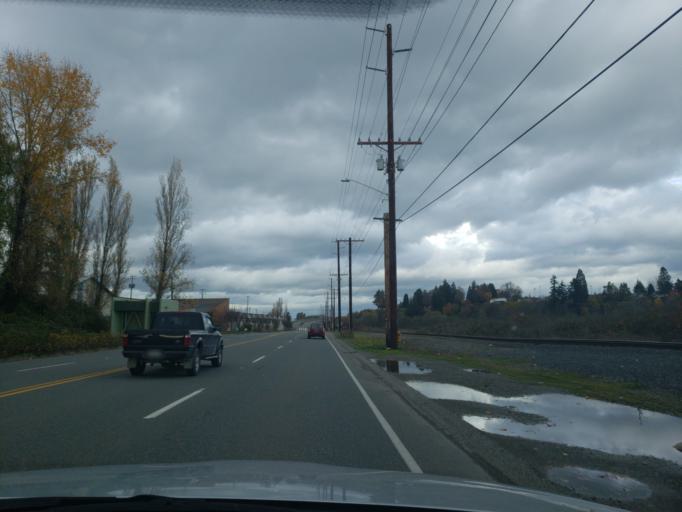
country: US
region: Washington
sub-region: Snohomish County
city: Everett
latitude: 48.0118
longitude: -122.2113
